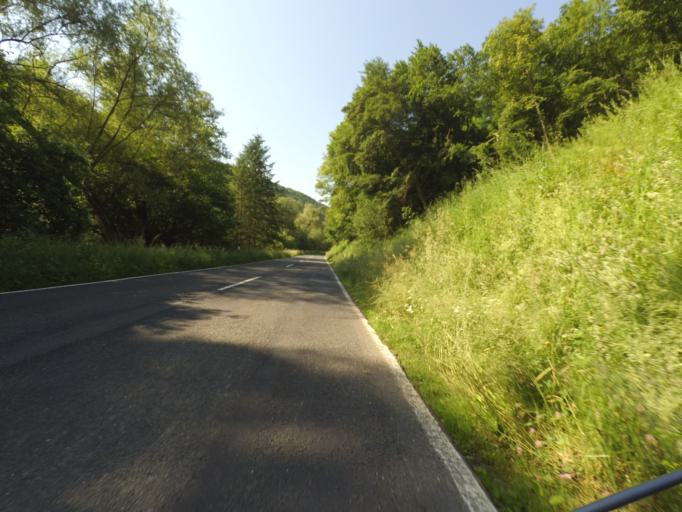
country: DE
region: Rheinland-Pfalz
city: Pommern
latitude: 50.1576
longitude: 7.2826
